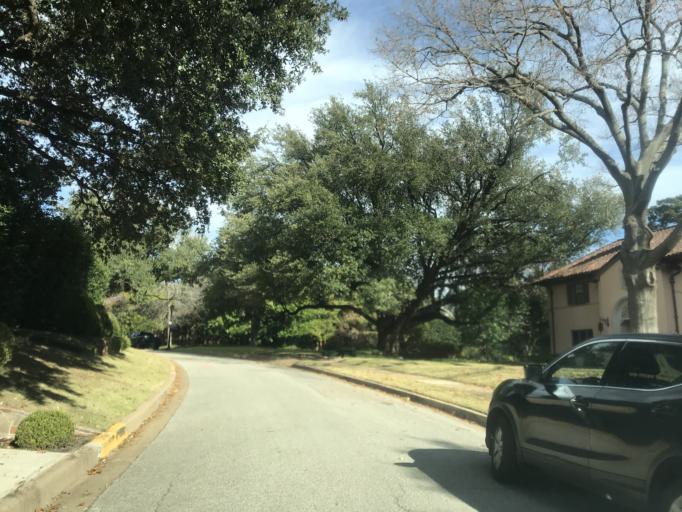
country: US
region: Texas
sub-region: Dallas County
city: Highland Park
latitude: 32.8205
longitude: -96.7986
